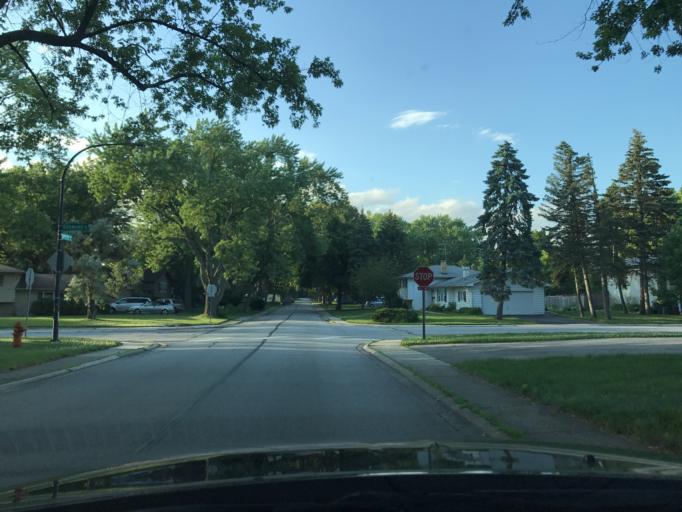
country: US
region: Illinois
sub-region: DuPage County
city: Naperville
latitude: 41.7526
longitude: -88.1568
